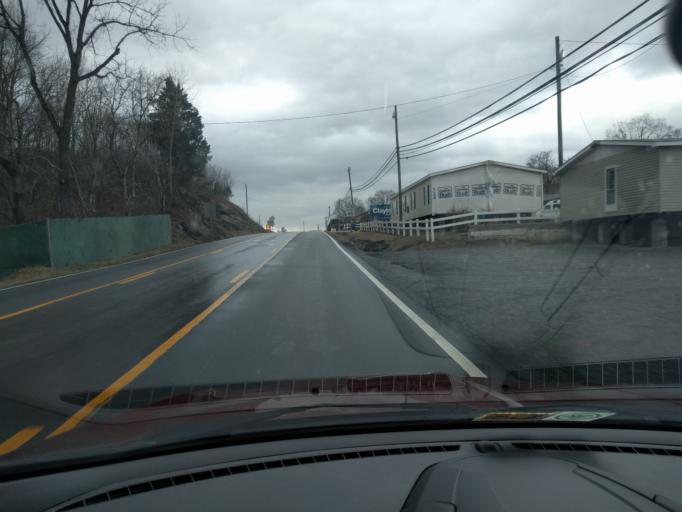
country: US
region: Virginia
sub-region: Botetourt County
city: Cloverdale
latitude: 37.3688
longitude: -79.9094
